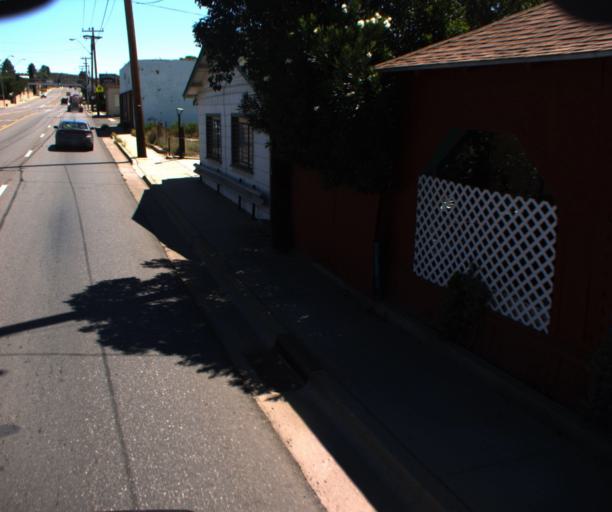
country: US
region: Arizona
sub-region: Gila County
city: Globe
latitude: 33.3936
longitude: -110.7795
